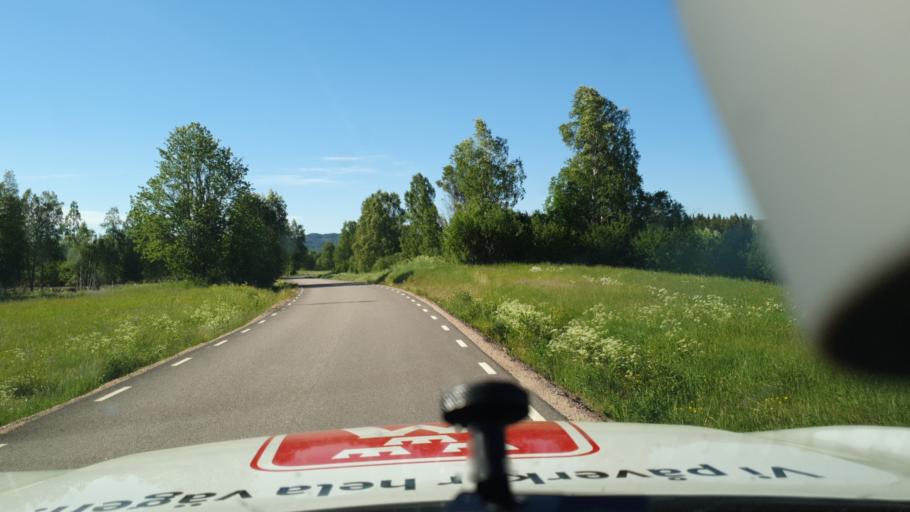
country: SE
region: Vaermland
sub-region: Torsby Kommun
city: Torsby
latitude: 60.2096
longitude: 13.0288
